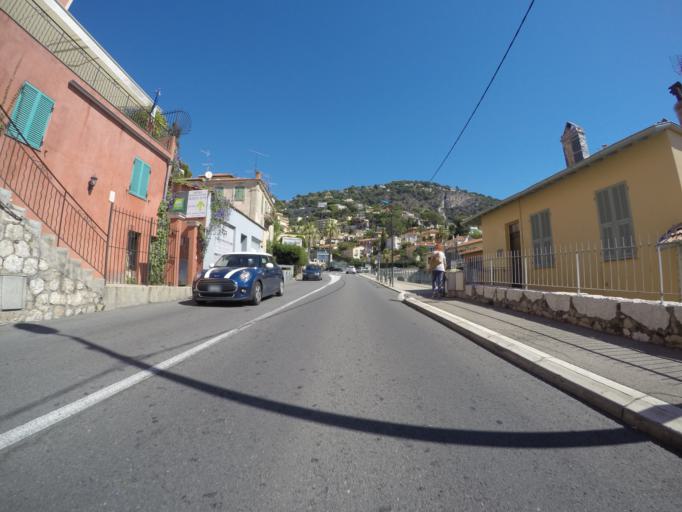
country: FR
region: Provence-Alpes-Cote d'Azur
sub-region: Departement des Alpes-Maritimes
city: Villefranche-sur-Mer
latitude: 43.7051
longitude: 7.3095
